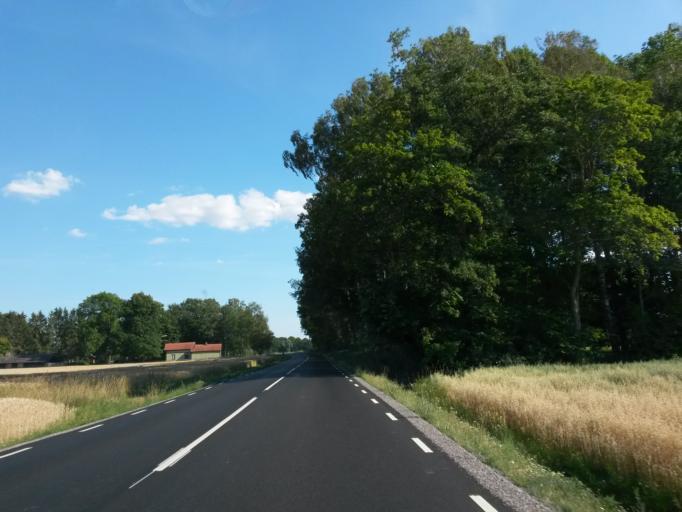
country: SE
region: Vaestra Goetaland
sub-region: Lidkopings Kommun
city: Lidkoping
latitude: 58.4678
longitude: 13.1437
